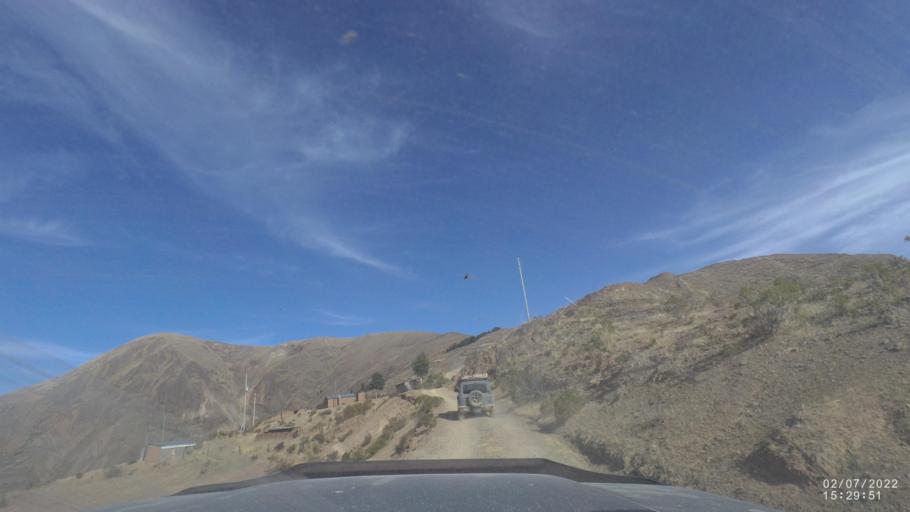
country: BO
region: Cochabamba
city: Irpa Irpa
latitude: -17.8798
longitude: -66.4139
